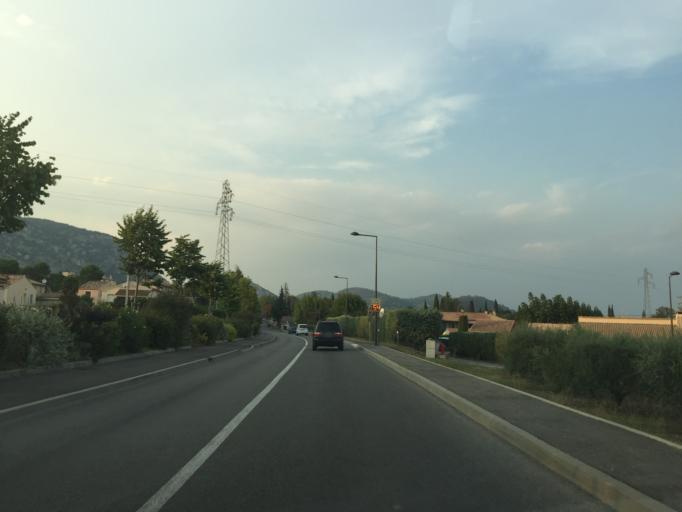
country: FR
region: Provence-Alpes-Cote d'Azur
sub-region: Departement des Alpes-de-Haute-Provence
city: Volx
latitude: 43.8684
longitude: 5.8430
